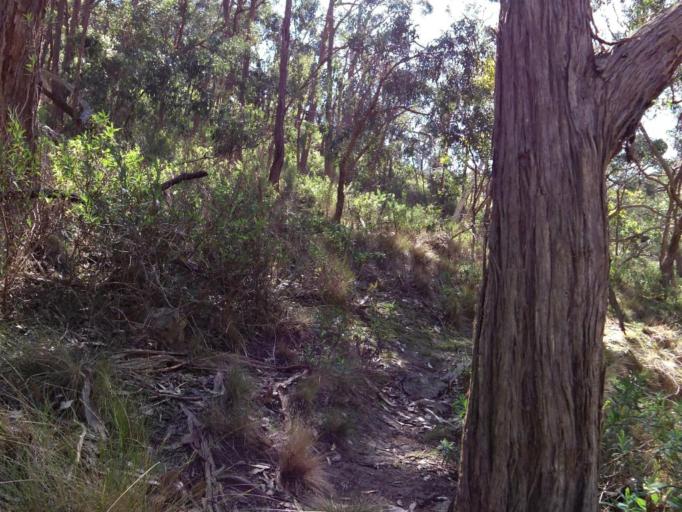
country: AU
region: Victoria
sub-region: Moorabool
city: Bacchus Marsh
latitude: -37.6686
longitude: 144.3177
